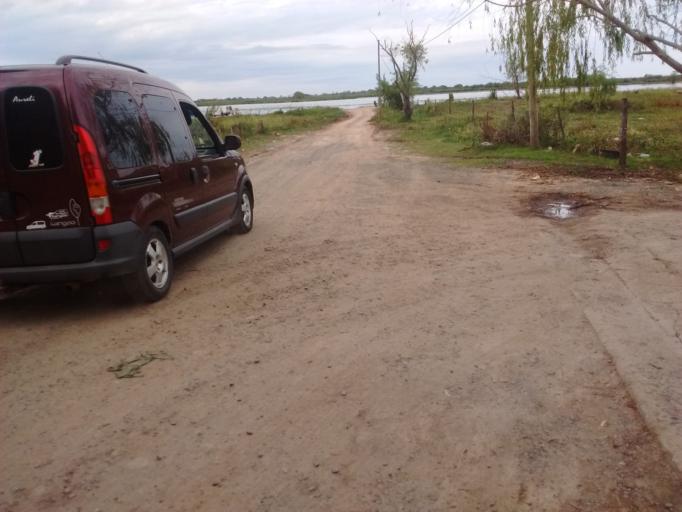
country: AR
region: Santa Fe
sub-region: Departamento de San Lorenzo
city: San Lorenzo
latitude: -32.4412
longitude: -60.8066
